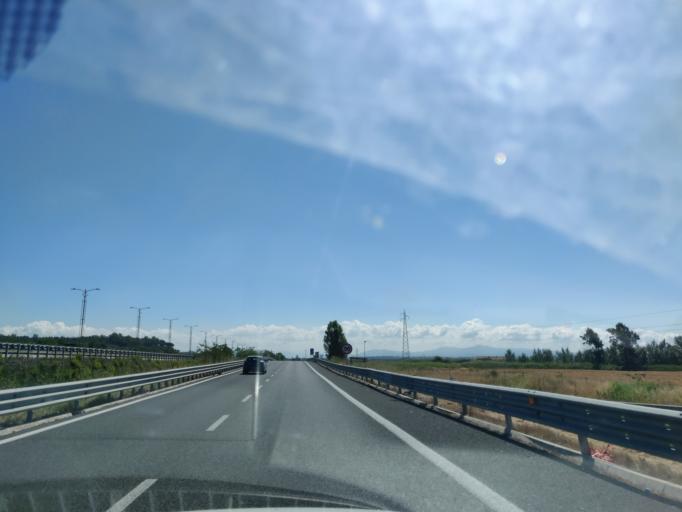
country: IT
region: Latium
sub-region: Citta metropolitana di Roma Capitale
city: Ponte Galeria-La Pisana
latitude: 41.8140
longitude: 12.3457
